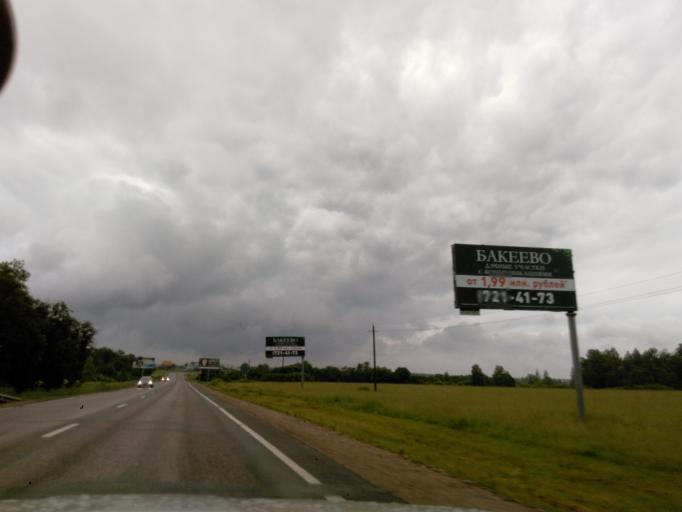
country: RU
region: Moskovskaya
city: Andreyevka
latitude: 55.9690
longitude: 37.0996
